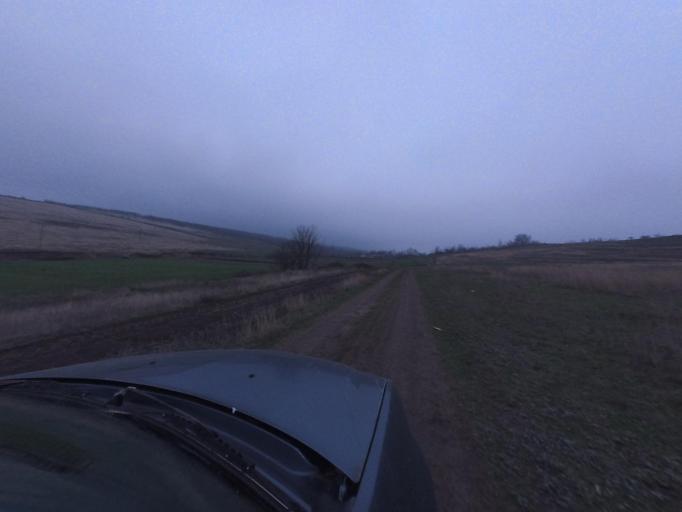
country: RO
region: Galati
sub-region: Comuna Balabanesti
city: Balabanesti
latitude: 46.1324
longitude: 27.7499
